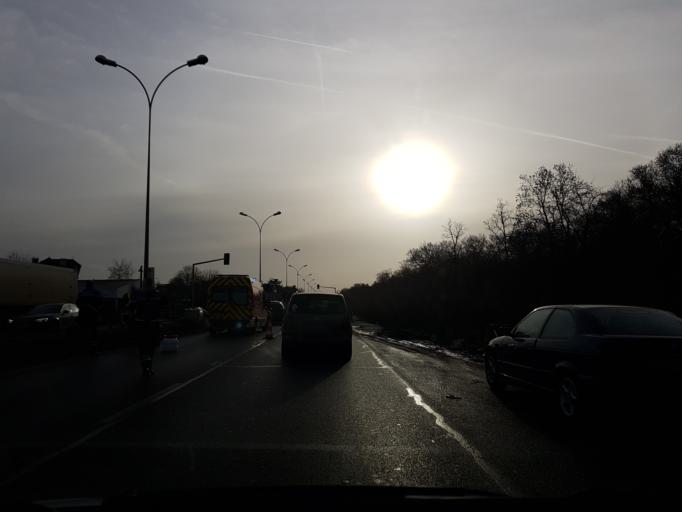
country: FR
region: Ile-de-France
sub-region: Departement de l'Essonne
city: Brunoy
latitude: 48.6819
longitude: 2.4918
